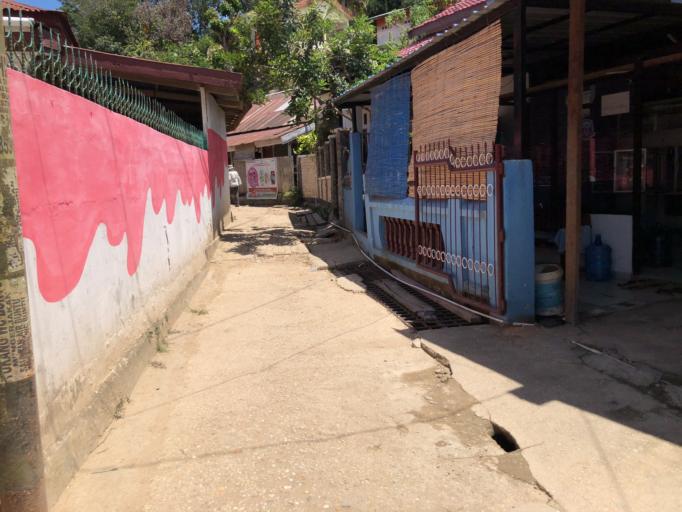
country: ID
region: Sulawesi Tenggara
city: Kendari
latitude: -3.9651
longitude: 122.5527
